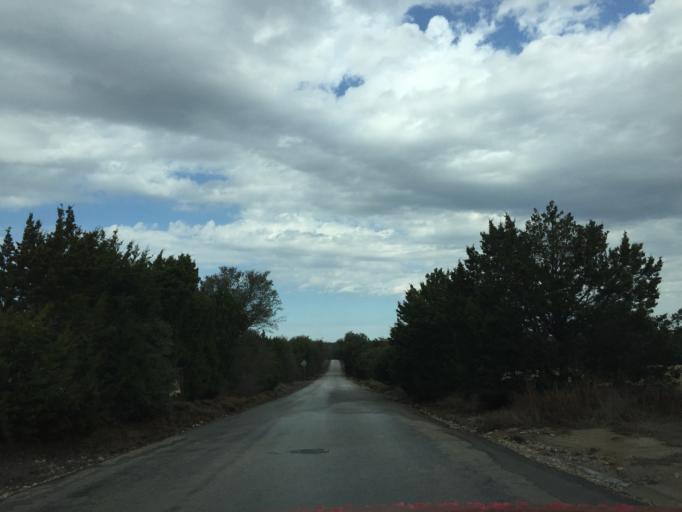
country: US
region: Texas
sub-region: Burnet County
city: Bertram
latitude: 30.6339
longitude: -98.0058
